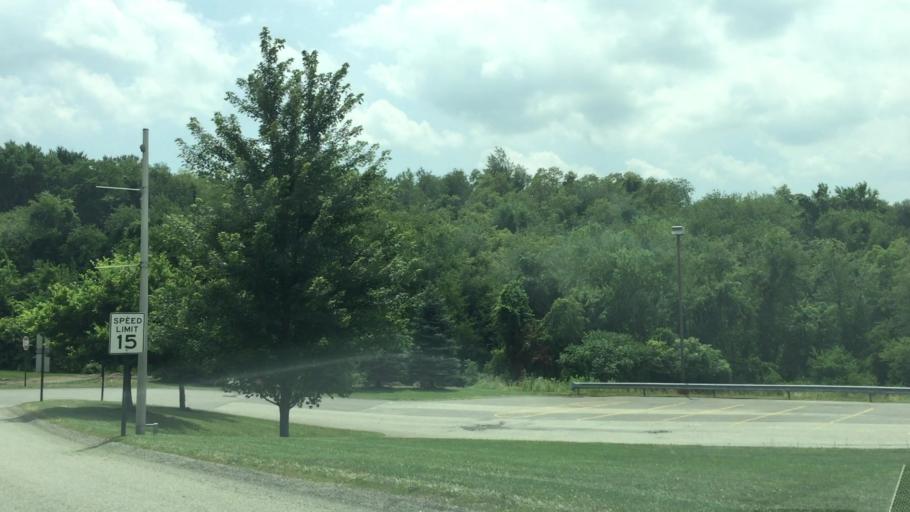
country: US
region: Pennsylvania
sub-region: Allegheny County
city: Imperial
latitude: 40.4472
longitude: -80.2391
